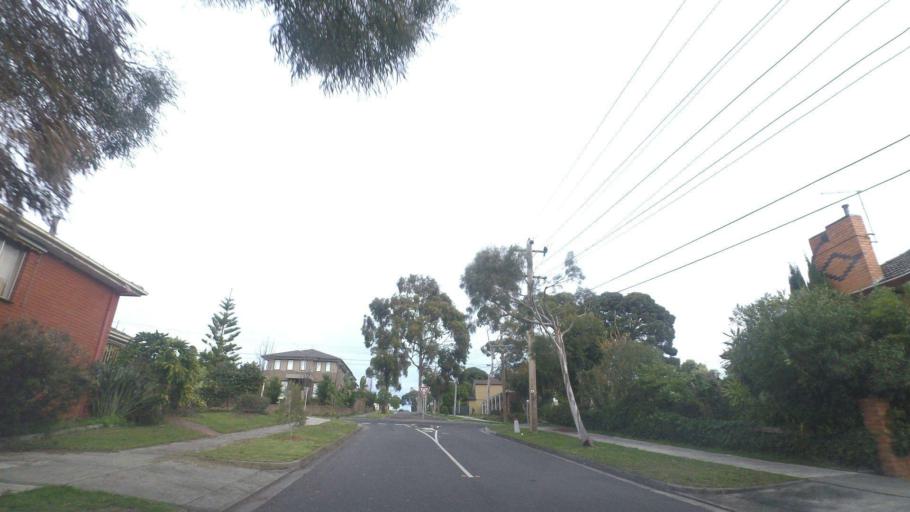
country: AU
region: Victoria
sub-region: Manningham
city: Bulleen
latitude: -37.7745
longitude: 145.0864
